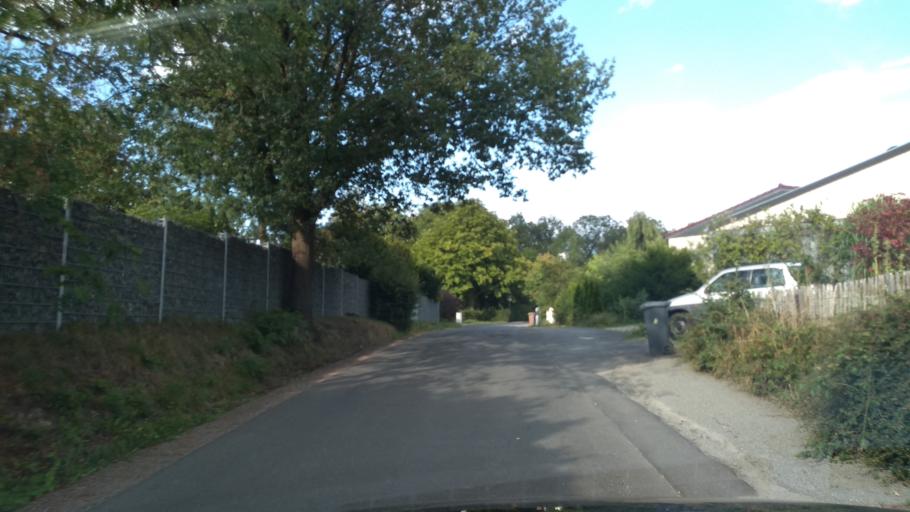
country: DE
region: North Rhine-Westphalia
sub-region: Regierungsbezirk Koln
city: Much
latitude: 50.8768
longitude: 7.3840
